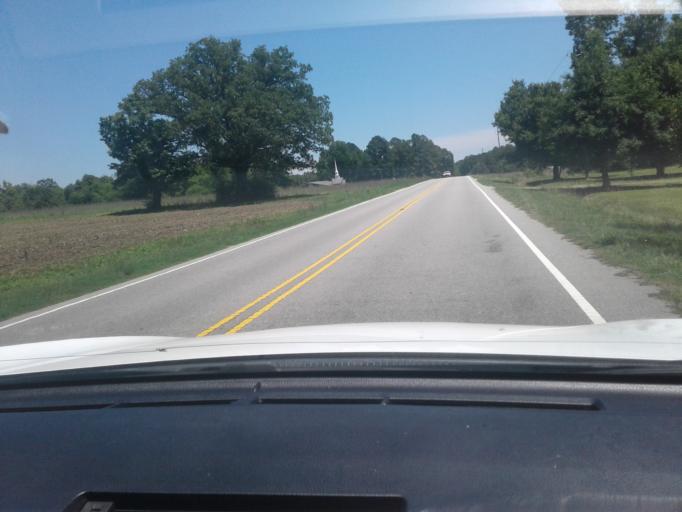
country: US
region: North Carolina
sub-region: Harnett County
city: Lillington
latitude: 35.3719
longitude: -78.8732
